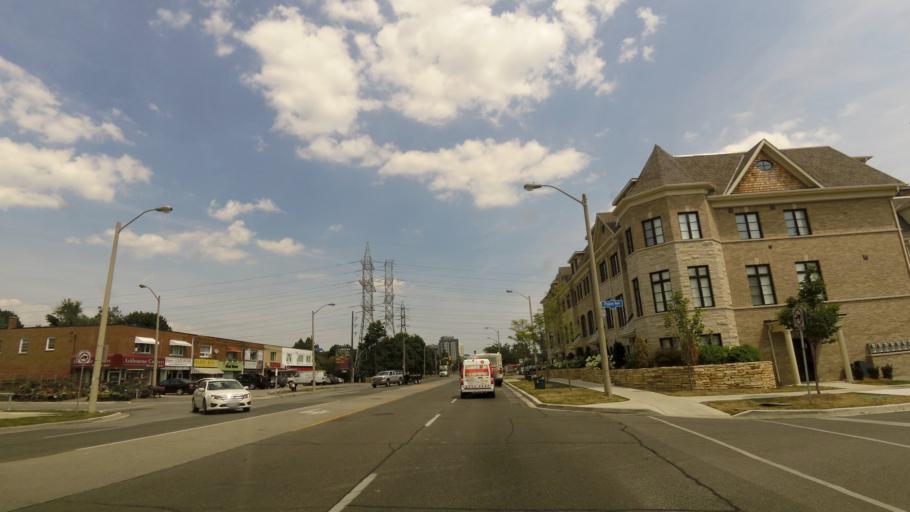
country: CA
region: Ontario
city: Etobicoke
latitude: 43.6402
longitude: -79.5426
